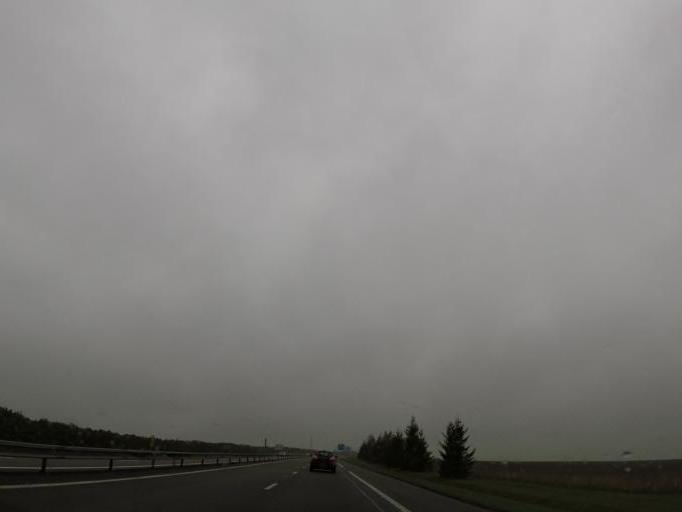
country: FR
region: Champagne-Ardenne
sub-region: Departement de la Marne
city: Courtisols
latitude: 49.0339
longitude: 4.4516
